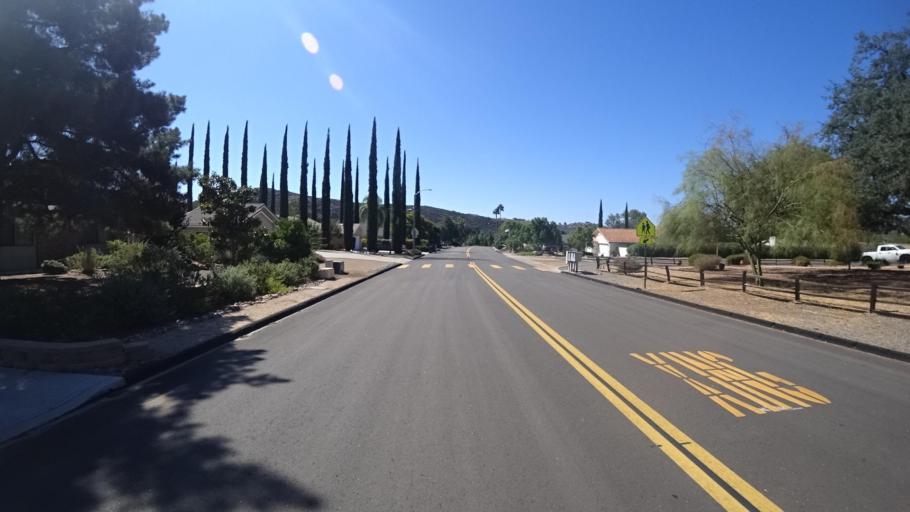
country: US
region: California
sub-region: San Diego County
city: San Diego Country Estates
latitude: 33.0159
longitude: -116.8072
